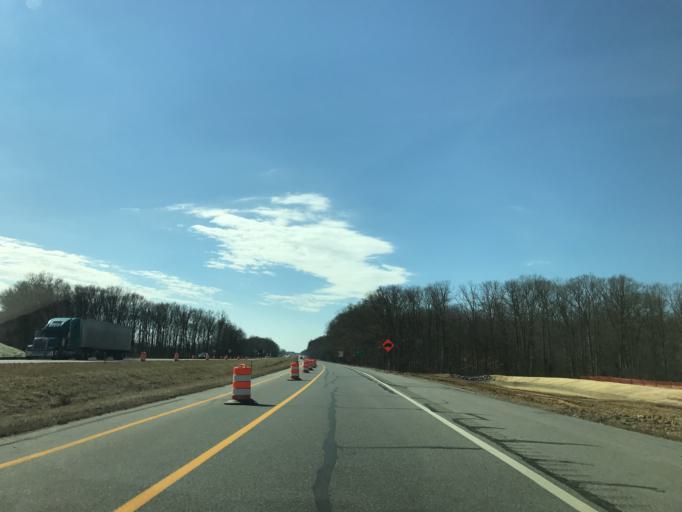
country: US
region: Delaware
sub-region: New Castle County
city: Middletown
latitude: 39.4100
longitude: -75.7719
